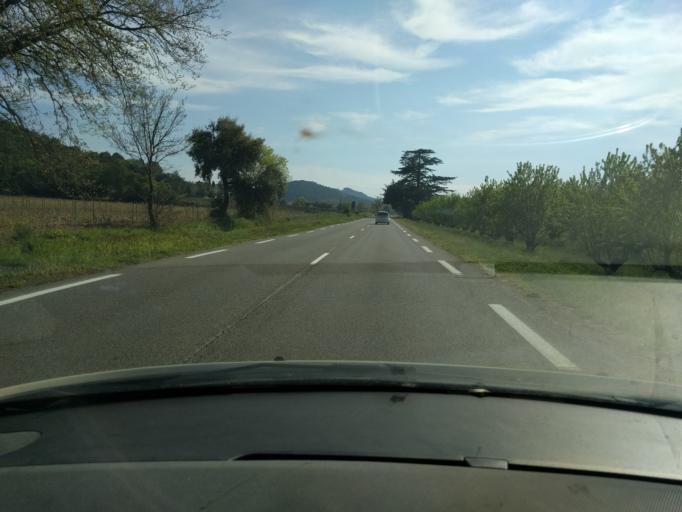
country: FR
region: Provence-Alpes-Cote d'Azur
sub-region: Departement du Var
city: Pierrefeu-du-Var
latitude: 43.1861
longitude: 6.1213
